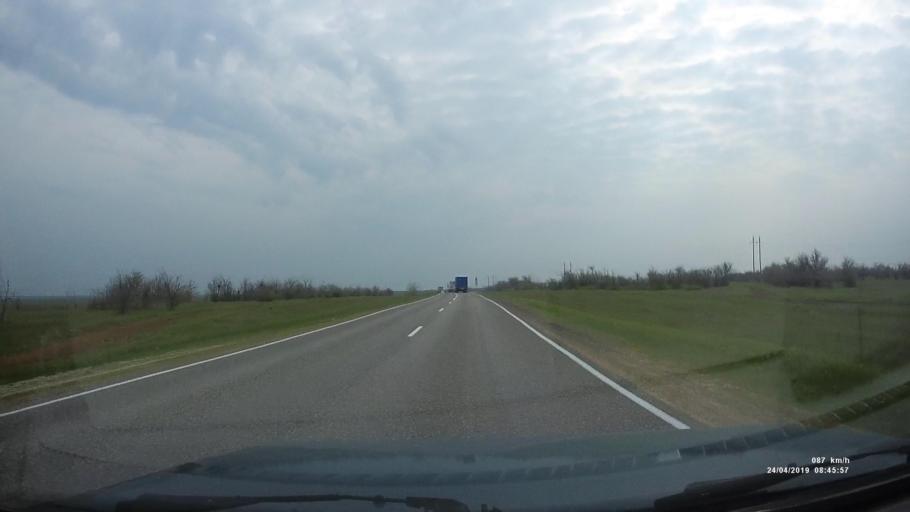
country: RU
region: Kalmykiya
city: Arshan'
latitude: 46.2364
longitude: 44.0705
